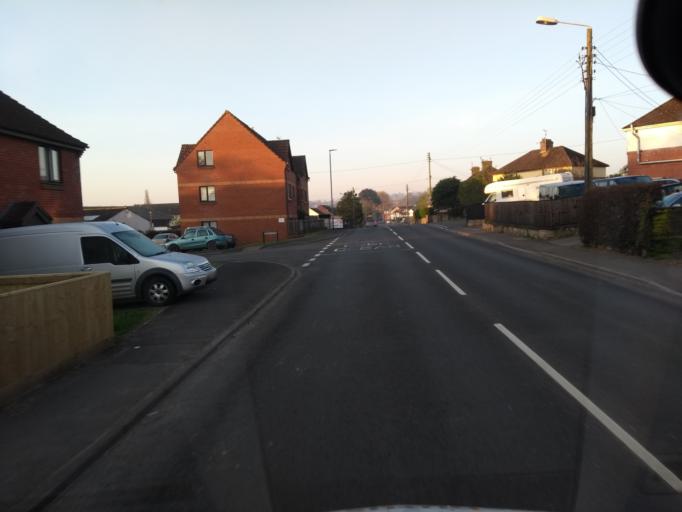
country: GB
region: England
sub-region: Somerset
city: Chard
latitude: 50.8820
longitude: -2.9541
